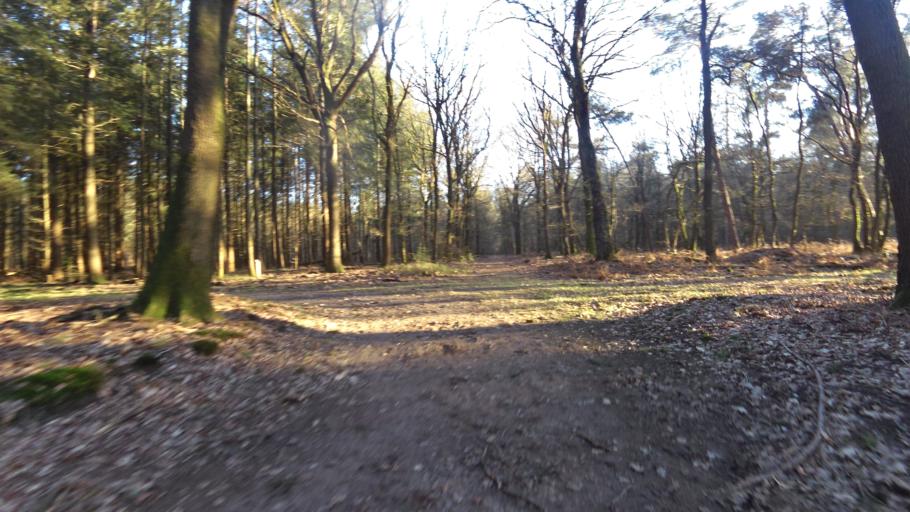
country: NL
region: Gelderland
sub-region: Gemeente Putten
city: Putten
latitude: 52.2579
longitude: 5.6412
